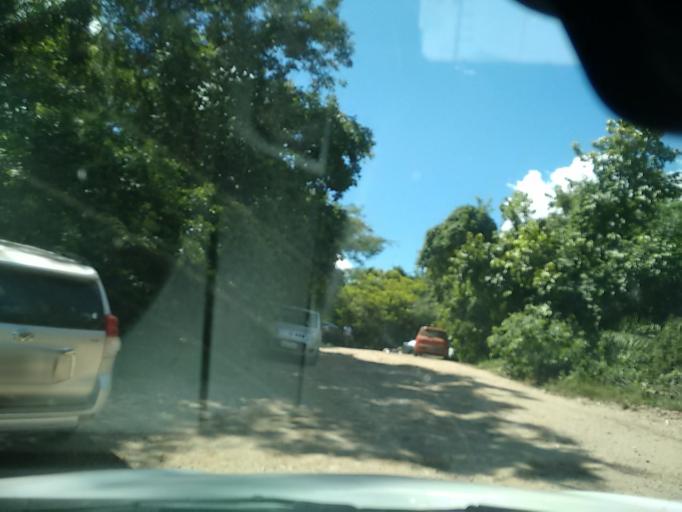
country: BR
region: Mato Grosso do Sul
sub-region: Bonito
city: Bonito
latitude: -21.1206
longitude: -56.3865
